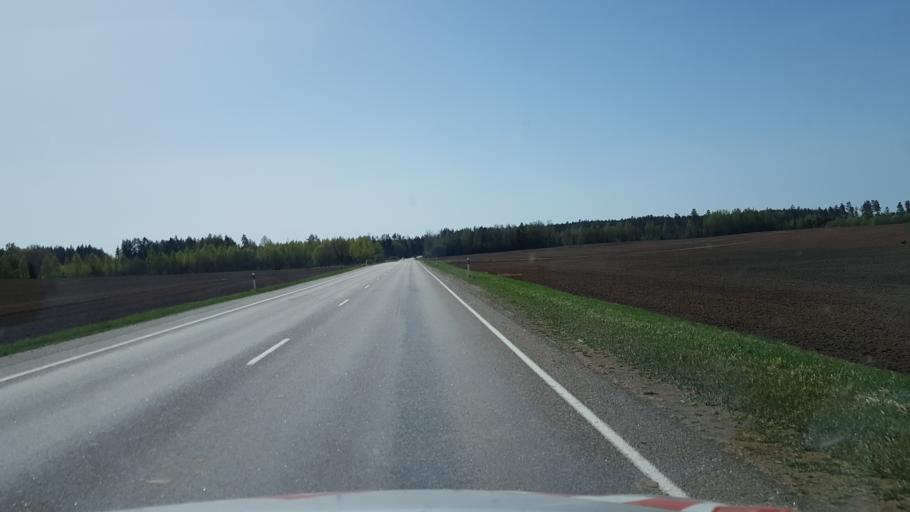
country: EE
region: Valgamaa
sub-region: Valga linn
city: Valga
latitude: 57.8626
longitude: 26.0580
